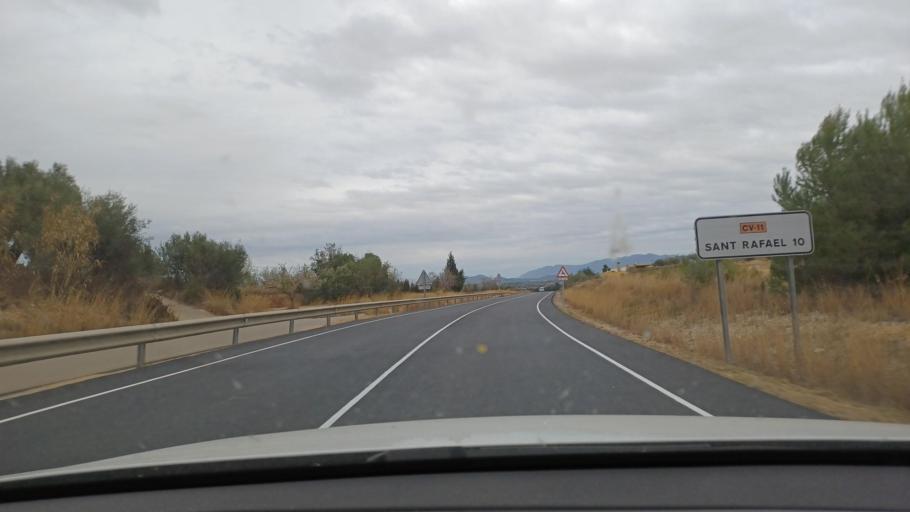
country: ES
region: Valencia
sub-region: Provincia de Castello
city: Traiguera
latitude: 40.5294
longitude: 0.2954
